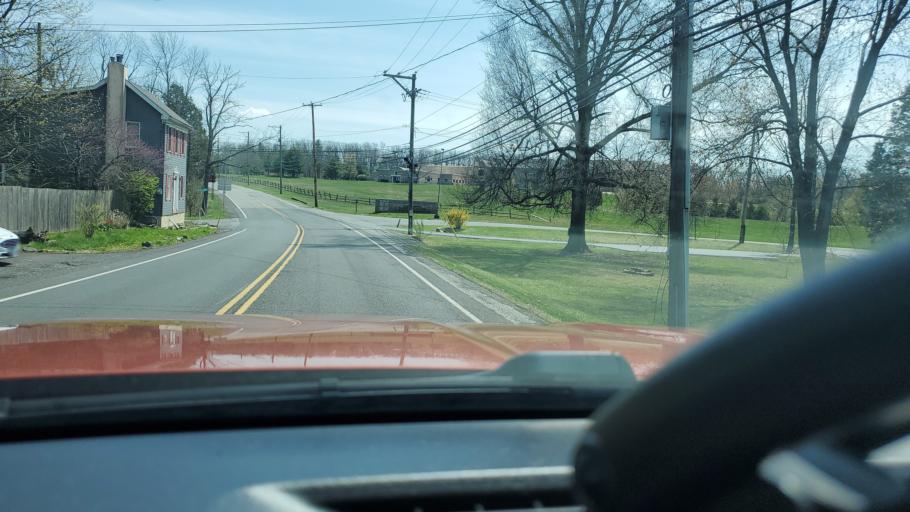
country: US
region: Pennsylvania
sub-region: Montgomery County
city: Red Hill
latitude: 40.3483
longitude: -75.4807
